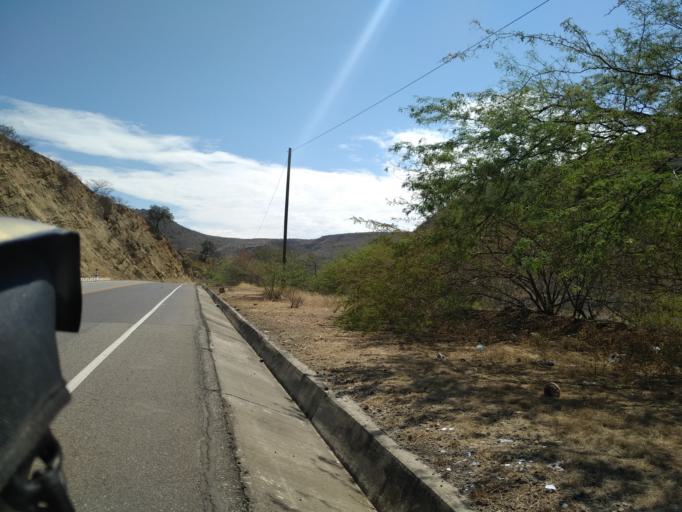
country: PE
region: Cajamarca
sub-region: Provincia de Cutervo
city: Choros
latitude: -5.8110
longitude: -78.7366
